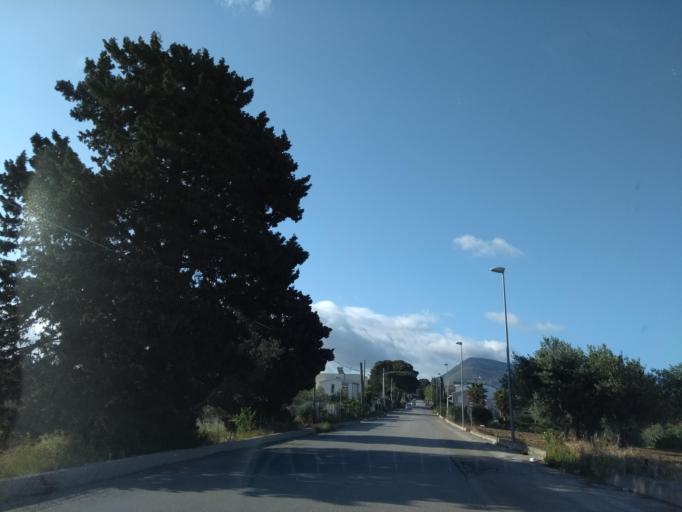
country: IT
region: Sicily
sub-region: Trapani
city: Alcamo
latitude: 38.0075
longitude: 12.9542
